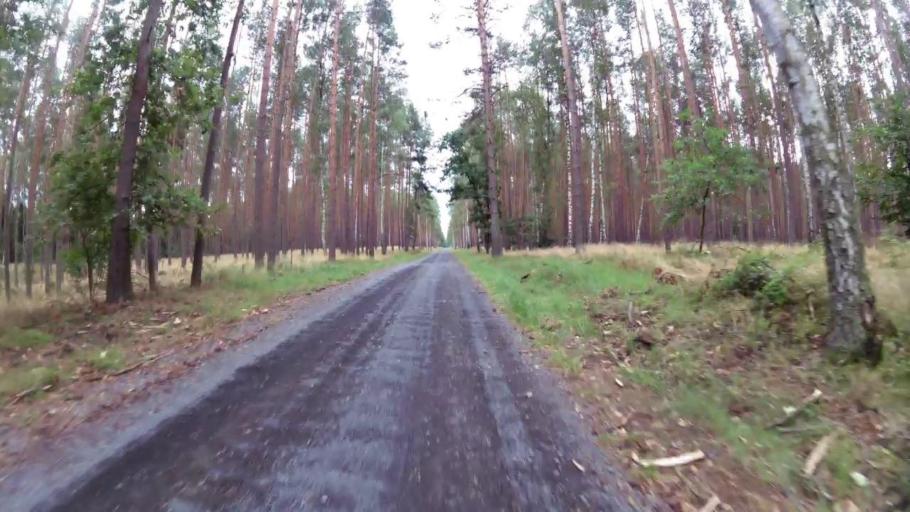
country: PL
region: West Pomeranian Voivodeship
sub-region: Powiat mysliborski
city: Debno
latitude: 52.7966
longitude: 14.7131
